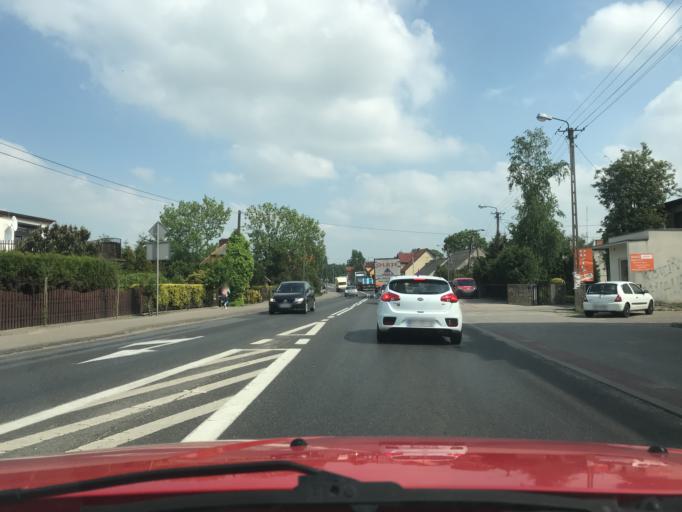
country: PL
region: Greater Poland Voivodeship
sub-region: Powiat jarocinski
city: Kotlin
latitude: 51.9189
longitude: 17.6484
